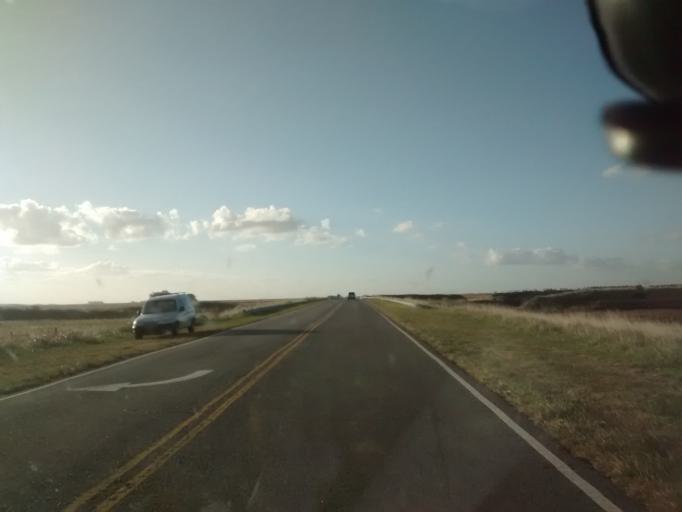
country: AR
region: Buenos Aires
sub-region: Partido de General Belgrano
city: General Belgrano
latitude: -36.0925
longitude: -58.6099
